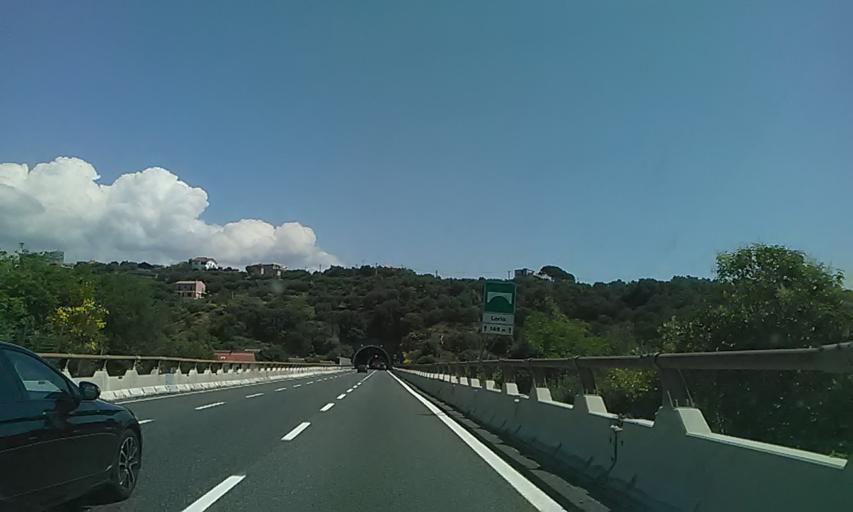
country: IT
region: Liguria
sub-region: Provincia di Savona
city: Celle Ligure
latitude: 44.3384
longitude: 8.5348
